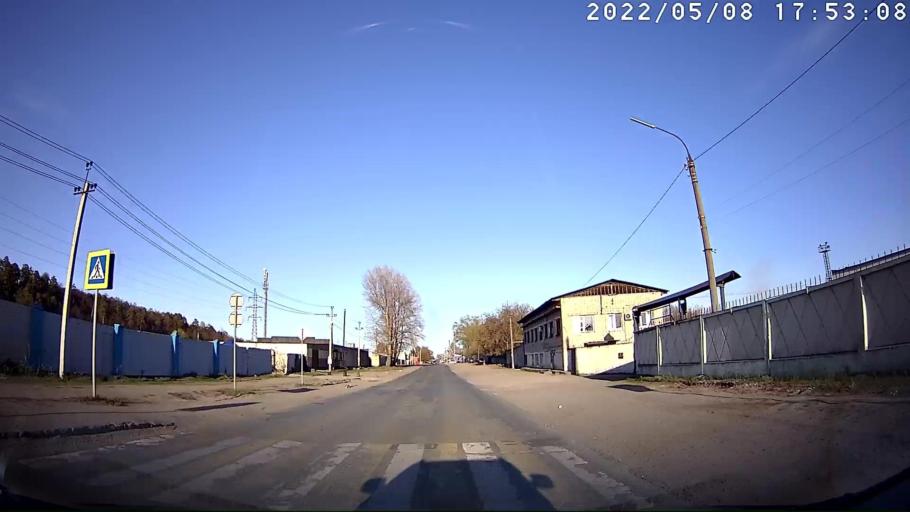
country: RU
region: Tatarstan
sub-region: Zelenodol'skiy Rayon
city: Zelenodolsk
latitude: 55.8400
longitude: 48.5133
